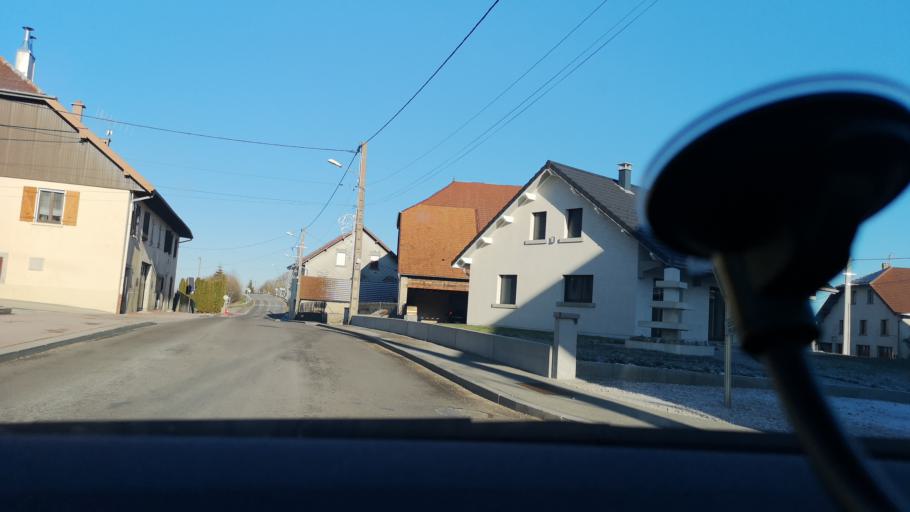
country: FR
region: Franche-Comte
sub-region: Departement du Doubs
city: Frasne
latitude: 46.8575
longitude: 6.1635
